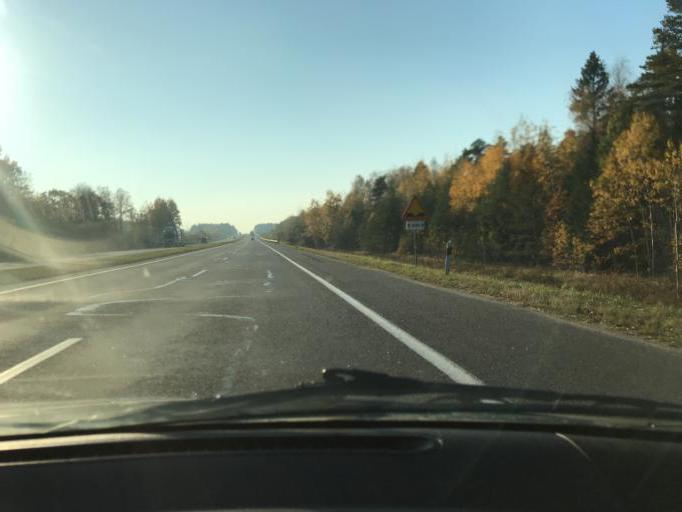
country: BY
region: Minsk
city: Loshnitsa
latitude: 54.2981
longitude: 28.9173
